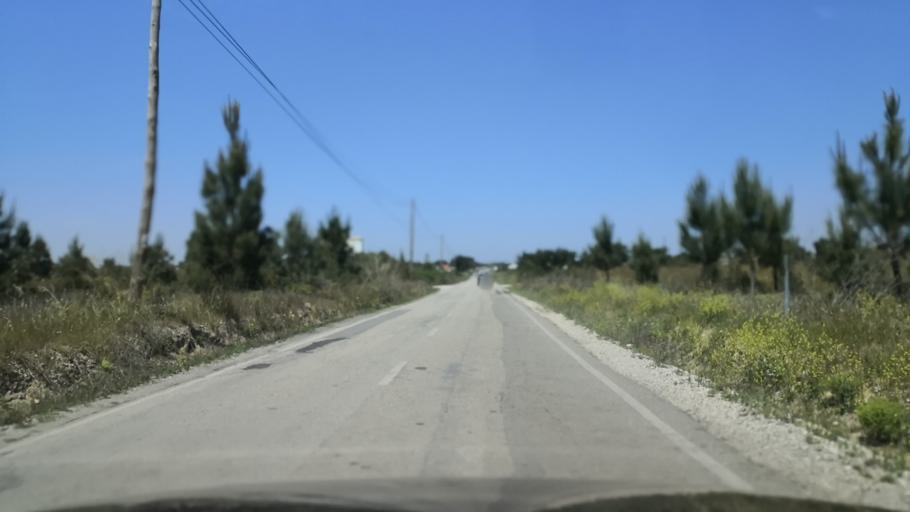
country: PT
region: Setubal
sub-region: Palmela
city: Palmela
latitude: 38.6276
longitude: -8.7467
